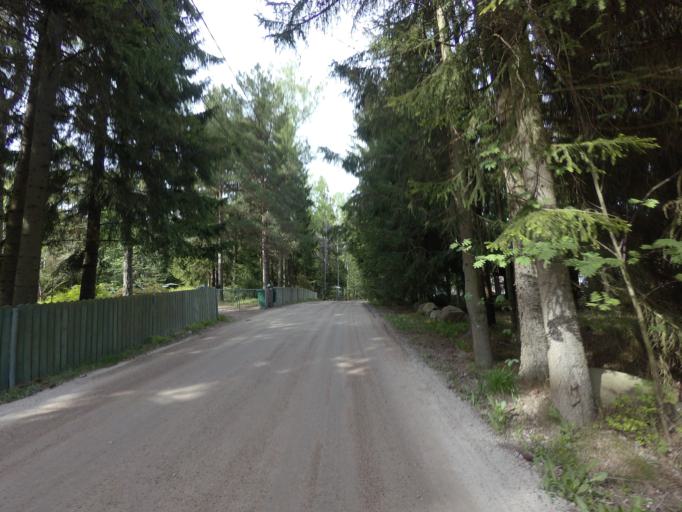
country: FI
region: Uusimaa
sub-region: Helsinki
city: Koukkuniemi
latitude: 60.1189
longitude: 24.7286
